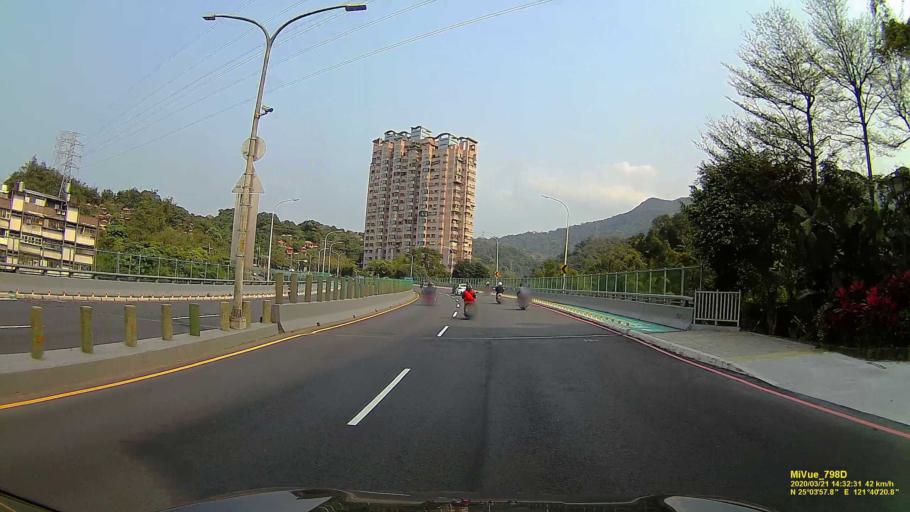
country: TW
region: Taiwan
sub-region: Keelung
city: Keelung
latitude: 25.0659
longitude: 121.6726
